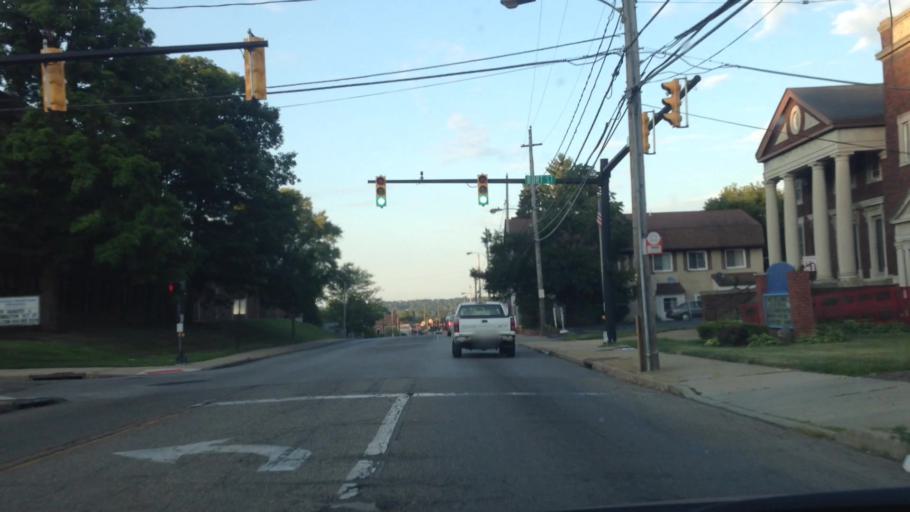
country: US
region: Ohio
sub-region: Summit County
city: Barberton
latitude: 41.0274
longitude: -81.5910
